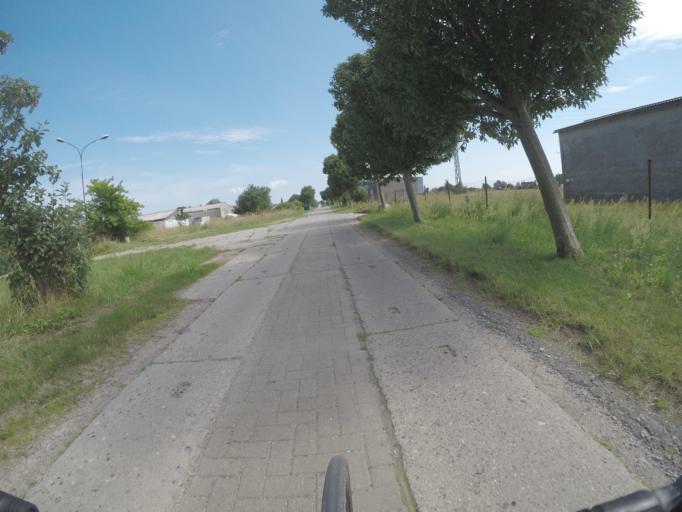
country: DE
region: Mecklenburg-Vorpommern
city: Rambin
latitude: 54.3569
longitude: 13.1970
